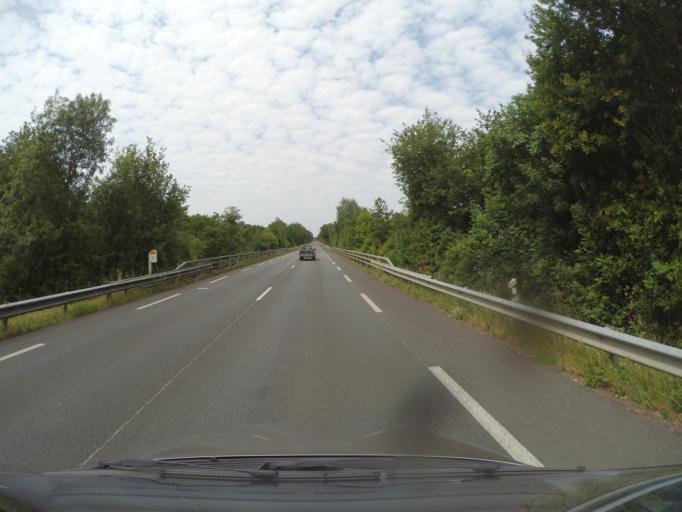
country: FR
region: Pays de la Loire
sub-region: Departement de la Vendee
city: Saint-Georges-de-Montaigu
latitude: 46.9360
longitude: -1.2911
